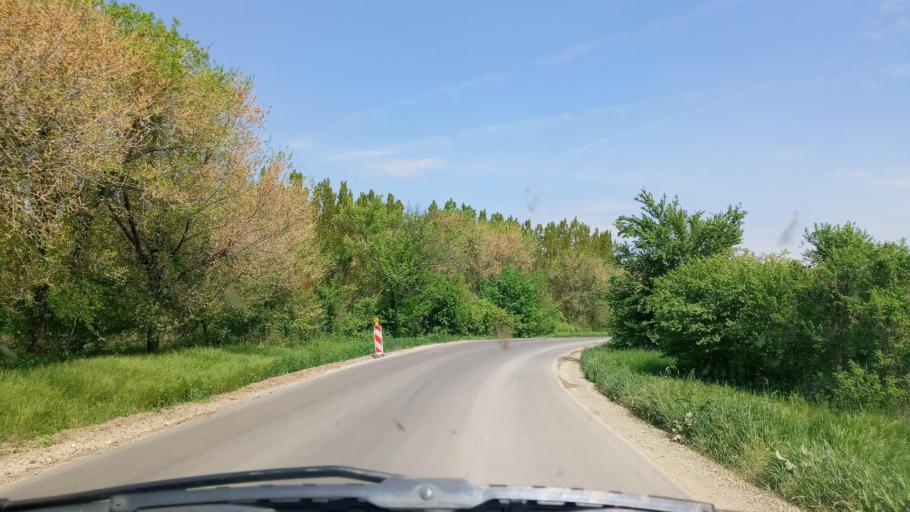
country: HU
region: Baranya
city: Boly
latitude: 45.9369
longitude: 18.5407
